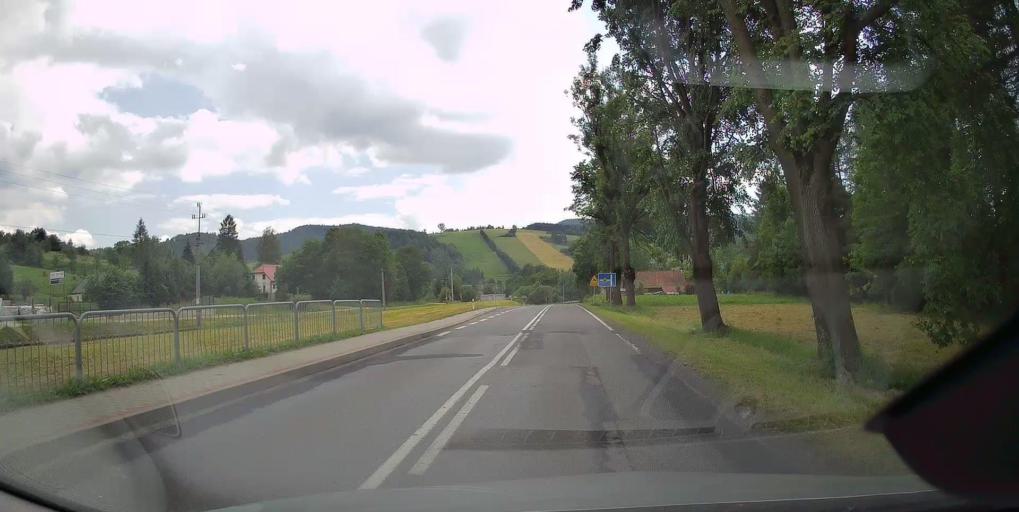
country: PL
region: Lesser Poland Voivodeship
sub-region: Powiat nowosadecki
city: Krynica-Zdroj
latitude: 49.3752
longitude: 20.9503
